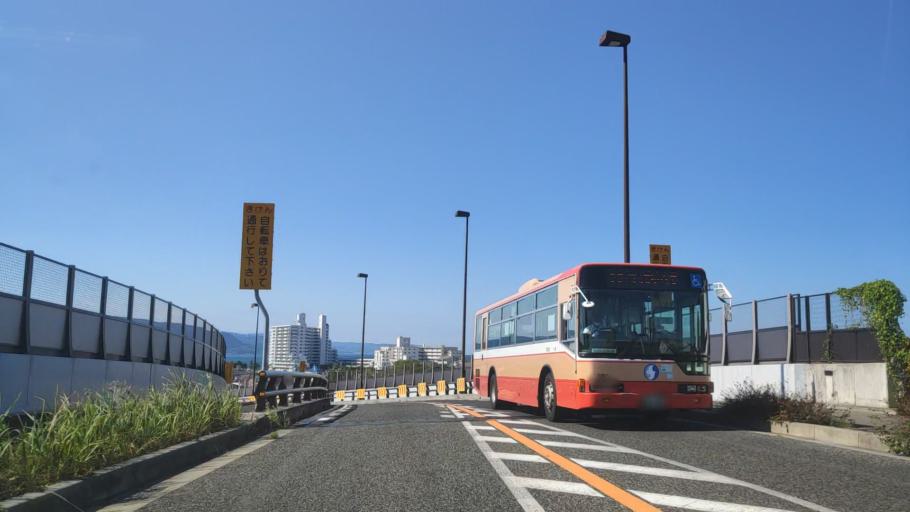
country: JP
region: Hyogo
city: Akashi
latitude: 34.6481
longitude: 135.0055
